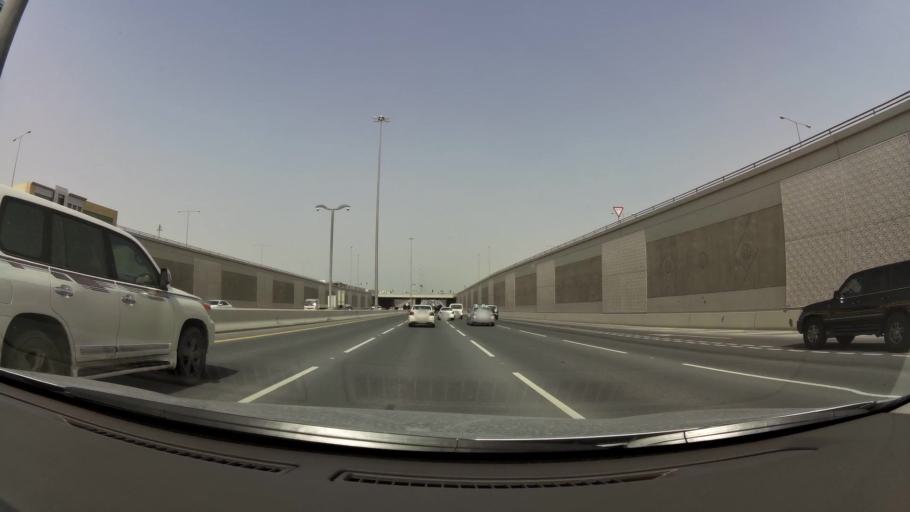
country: QA
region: Baladiyat ad Dawhah
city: Doha
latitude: 25.2477
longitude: 51.4696
